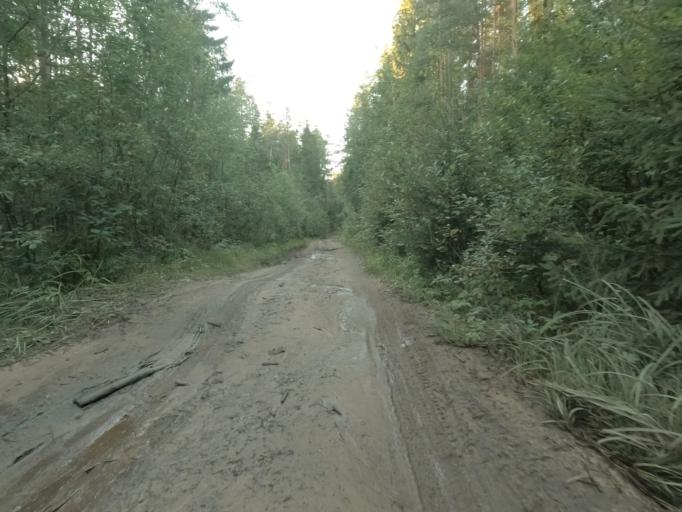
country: RU
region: Leningrad
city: Otradnoye
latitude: 59.8258
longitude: 30.8192
